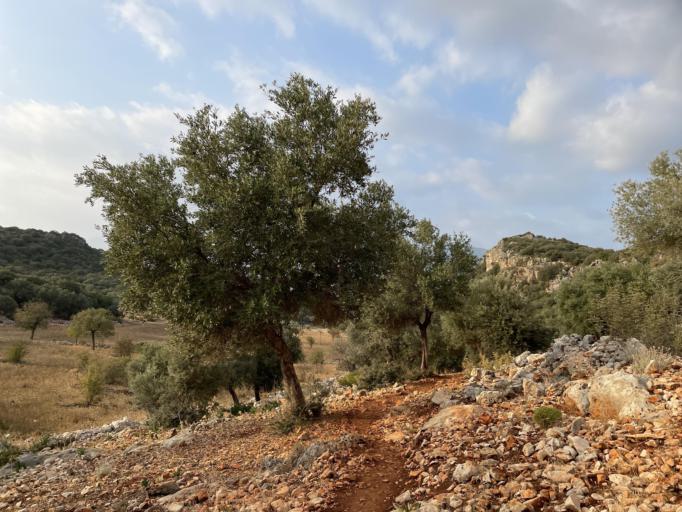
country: TR
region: Antalya
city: Kas
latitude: 36.1674
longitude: 29.6535
